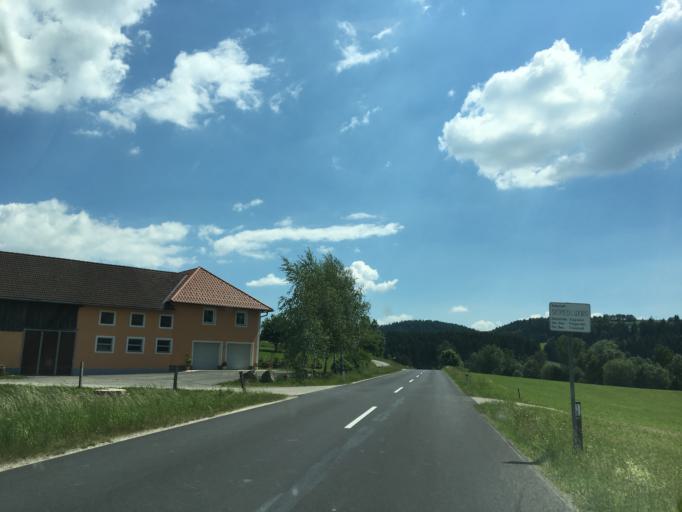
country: AT
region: Upper Austria
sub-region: Politischer Bezirk Perg
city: Perg
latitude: 48.3166
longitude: 14.6055
